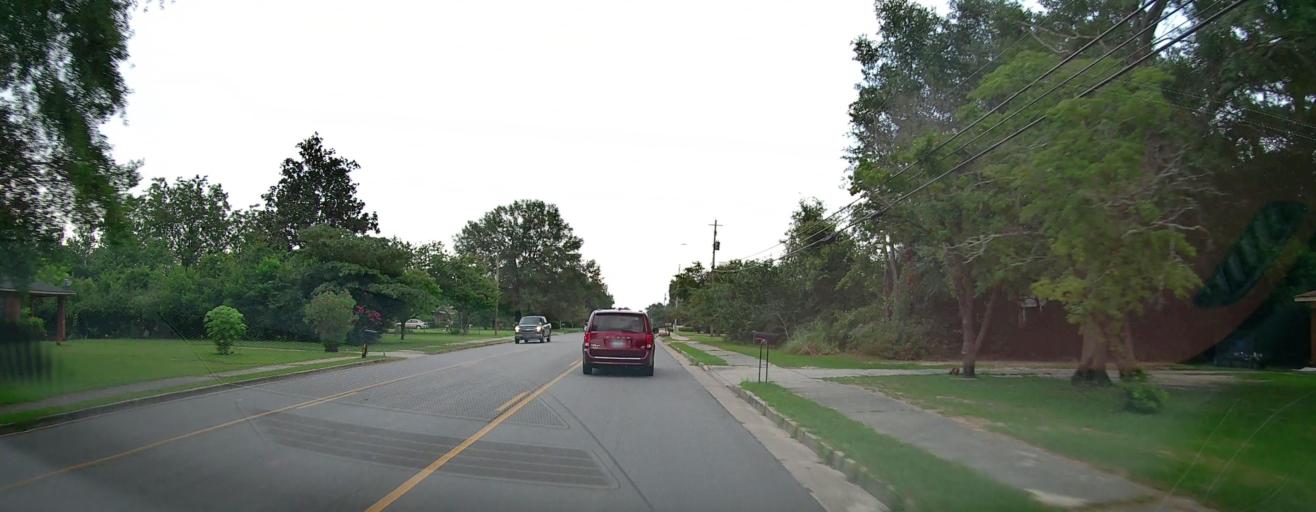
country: US
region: Georgia
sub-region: Laurens County
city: Dublin
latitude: 32.5613
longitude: -82.9133
